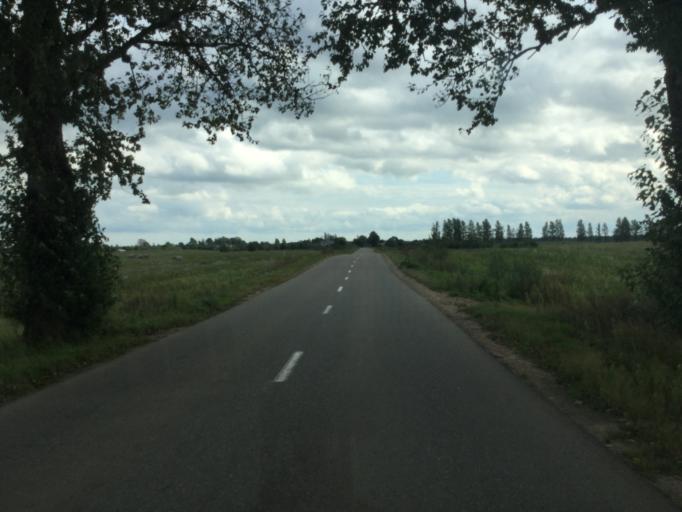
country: BY
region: Vitebsk
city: Vitebsk
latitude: 55.1525
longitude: 30.2733
